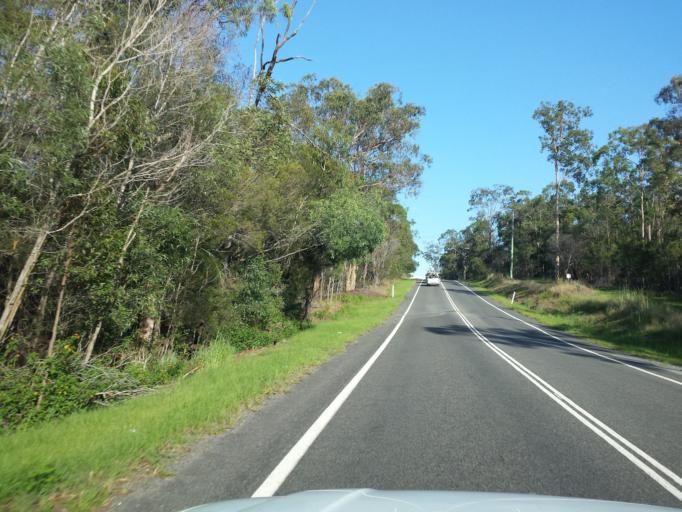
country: AU
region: Queensland
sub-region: Gold Coast
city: Ormeau Hills
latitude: -27.7732
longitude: 153.2250
